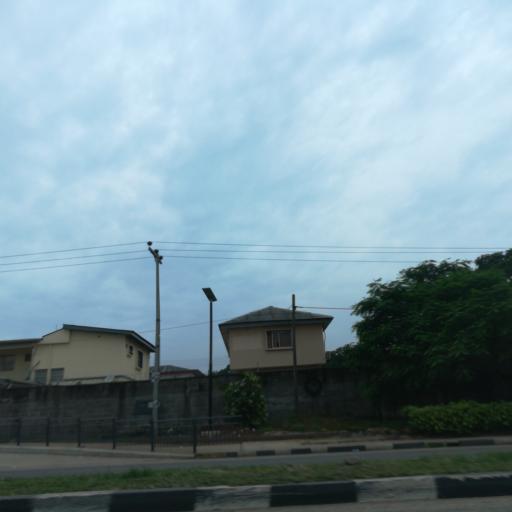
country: NG
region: Lagos
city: Ojota
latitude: 6.5781
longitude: 3.3609
